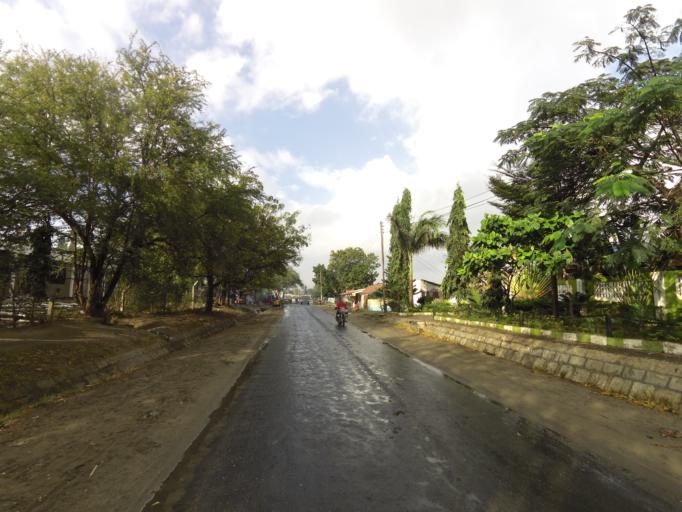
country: TZ
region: Dar es Salaam
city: Magomeni
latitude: -6.7864
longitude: 39.2353
